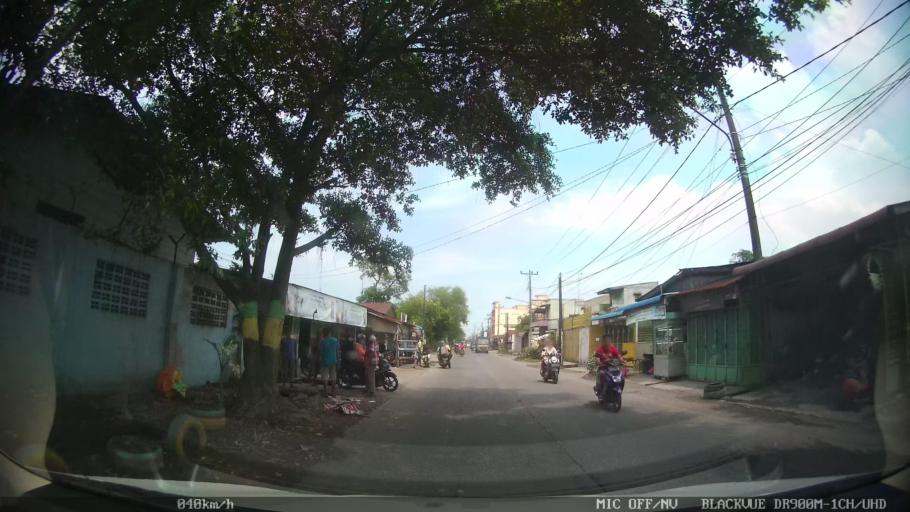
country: ID
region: North Sumatra
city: Labuhan Deli
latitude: 3.6572
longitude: 98.6671
